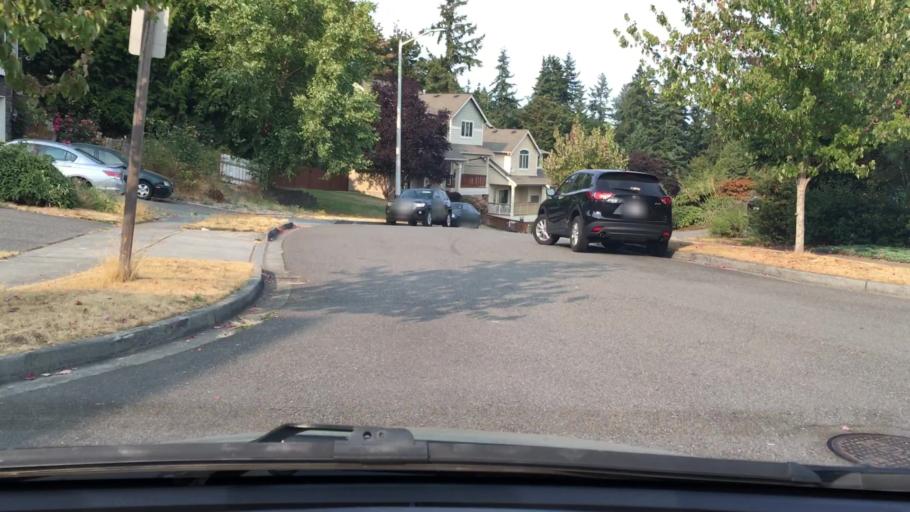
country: US
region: Washington
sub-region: Snohomish County
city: Martha Lake
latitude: 47.8528
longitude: -122.2509
